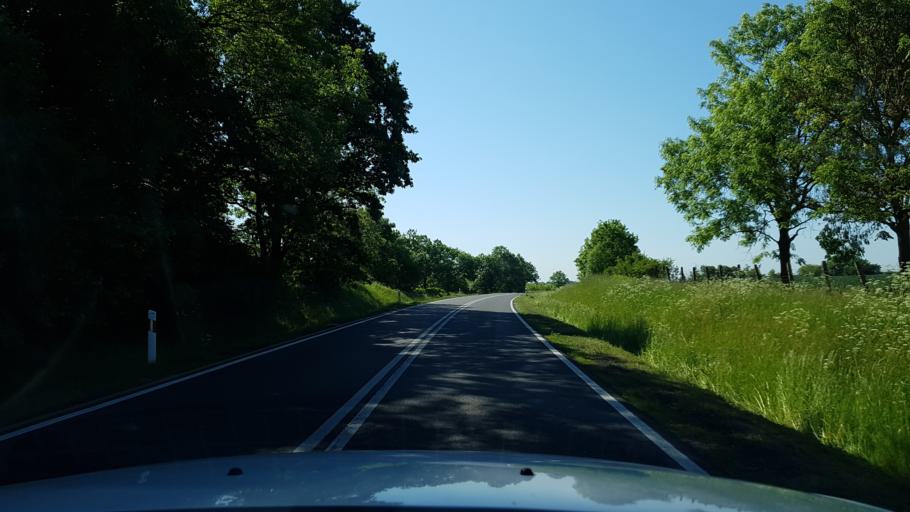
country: PL
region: West Pomeranian Voivodeship
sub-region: Powiat gryfinski
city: Mieszkowice
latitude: 52.8509
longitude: 14.4907
